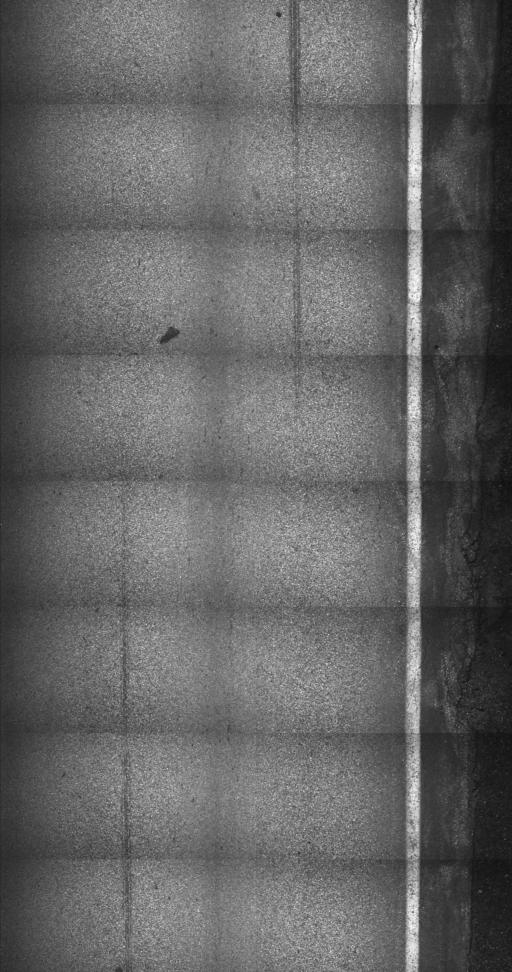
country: US
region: Vermont
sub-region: Rutland County
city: Rutland
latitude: 43.7231
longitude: -72.8227
